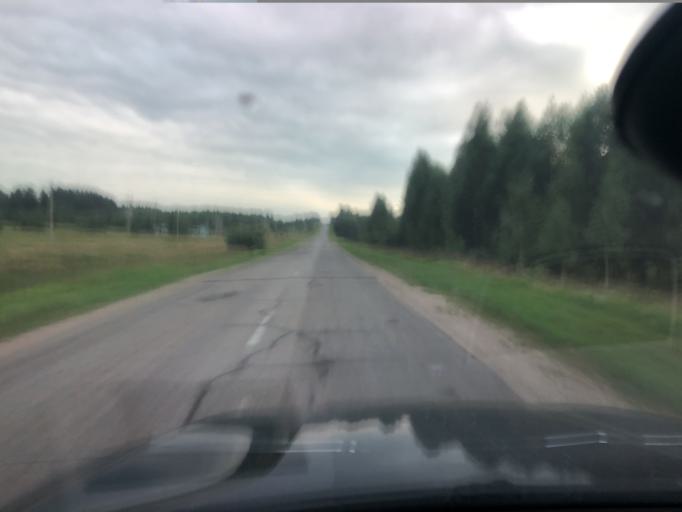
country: RU
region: Jaroslavl
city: Petrovsk
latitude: 57.0108
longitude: 39.0028
